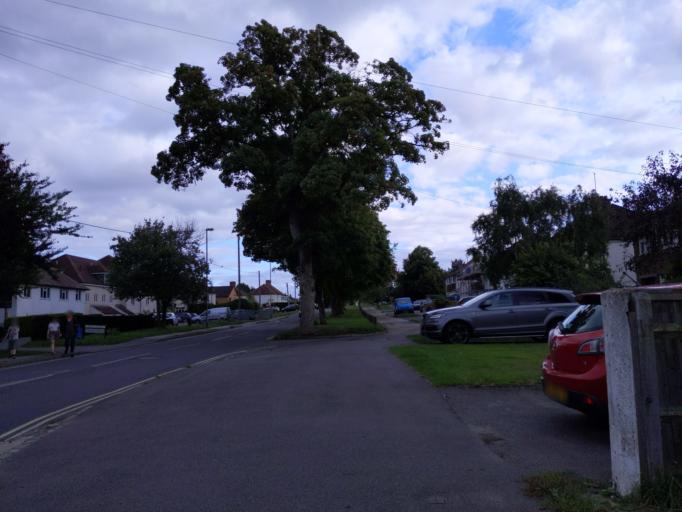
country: GB
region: England
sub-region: Oxfordshire
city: Radley
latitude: 51.7160
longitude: -1.2451
